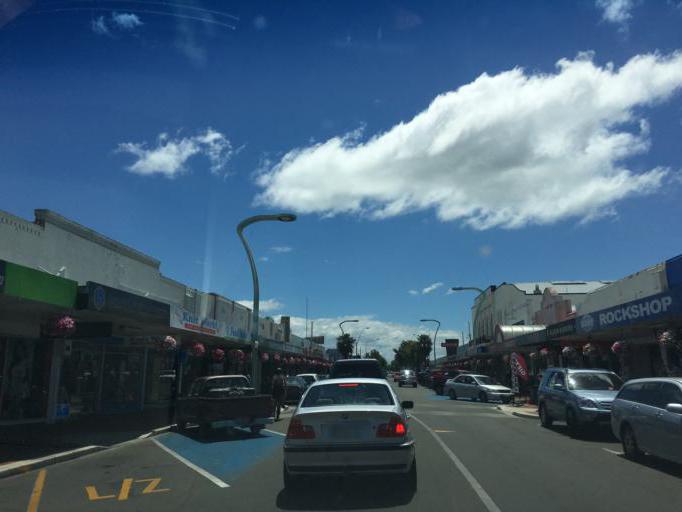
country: NZ
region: Hawke's Bay
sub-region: Hastings District
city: Hastings
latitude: -39.6397
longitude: 176.8409
